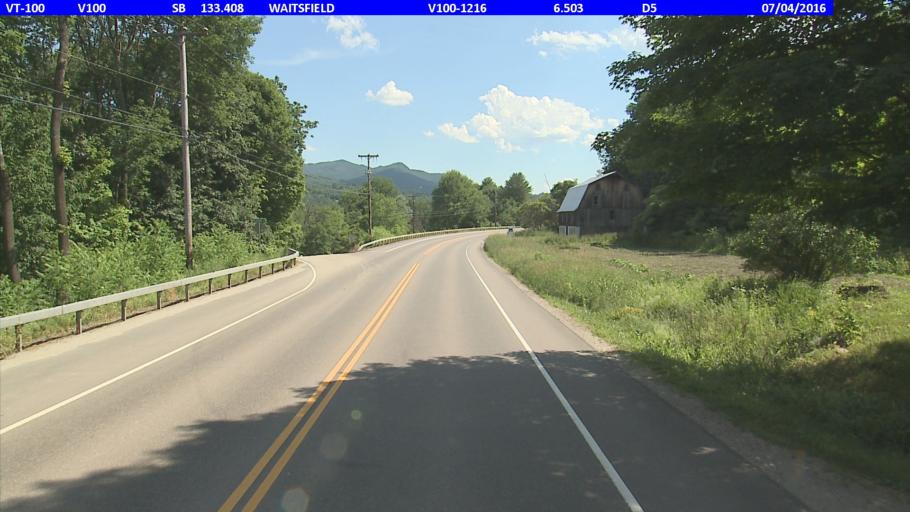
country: US
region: Vermont
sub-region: Washington County
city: Waterbury
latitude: 44.2214
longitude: -72.7899
